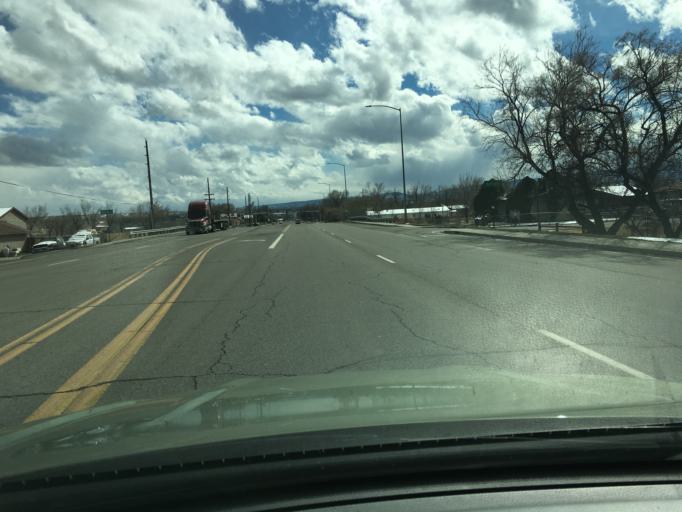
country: US
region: Colorado
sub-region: Mesa County
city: Clifton
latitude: 39.0802
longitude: -108.4595
